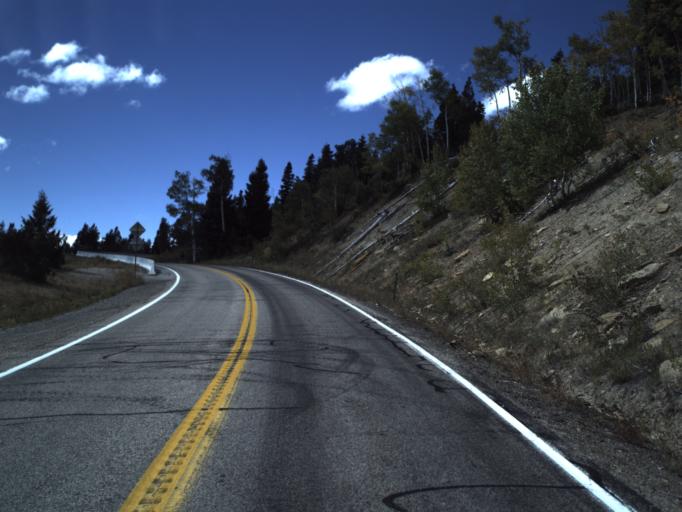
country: US
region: Utah
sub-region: Iron County
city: Cedar City
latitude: 37.5918
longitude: -112.8979
